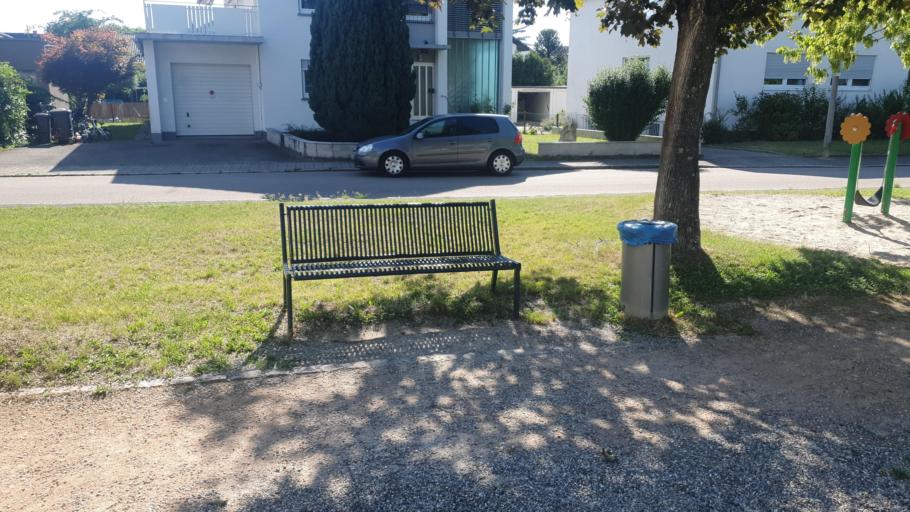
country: DE
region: Baden-Wuerttemberg
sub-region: Freiburg Region
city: Weil am Rhein
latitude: 47.5963
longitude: 7.6160
